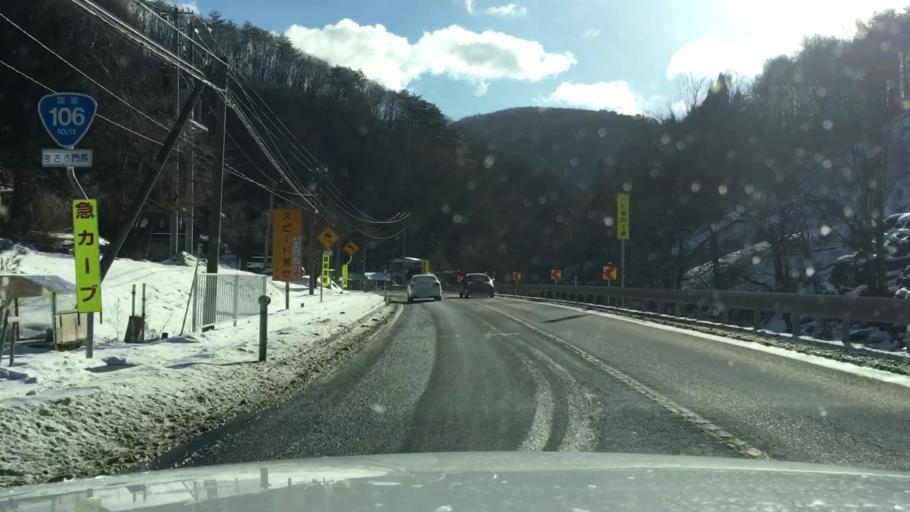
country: JP
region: Iwate
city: Tono
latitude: 39.6145
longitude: 141.4820
